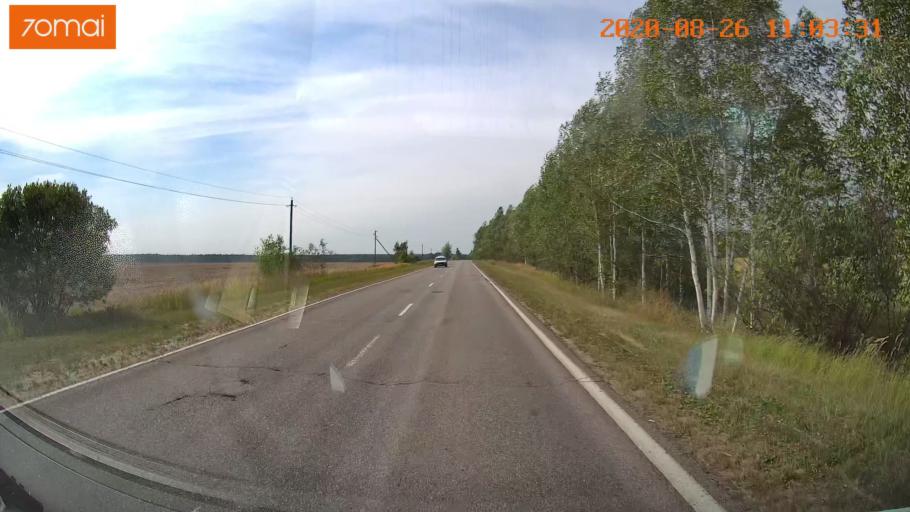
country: RU
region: Rjazan
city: Izhevskoye
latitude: 54.5400
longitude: 41.2101
